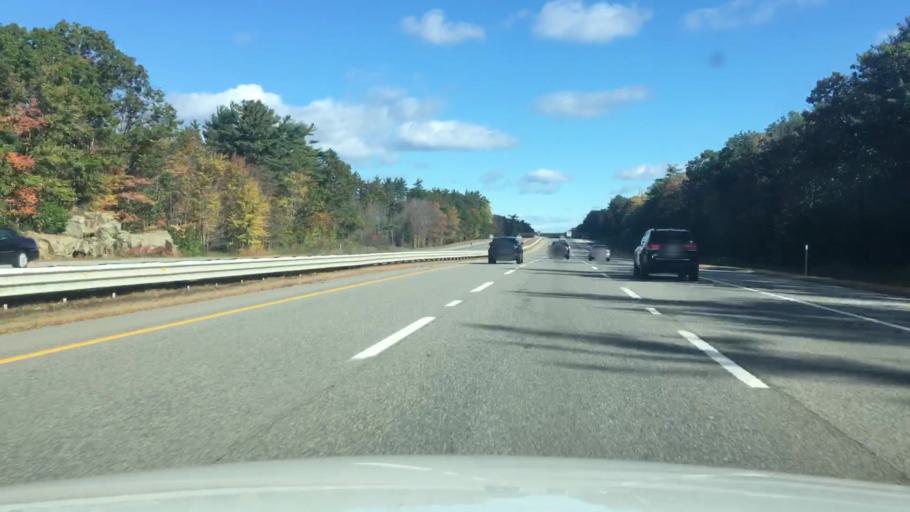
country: US
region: Maine
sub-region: York County
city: Ogunquit
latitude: 43.2418
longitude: -70.6290
